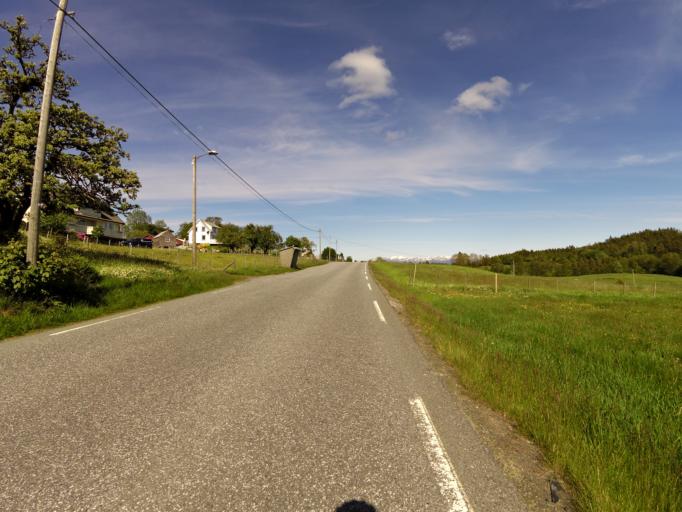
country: NO
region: Hordaland
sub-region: Stord
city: Leirvik
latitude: 59.7863
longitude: 5.4610
